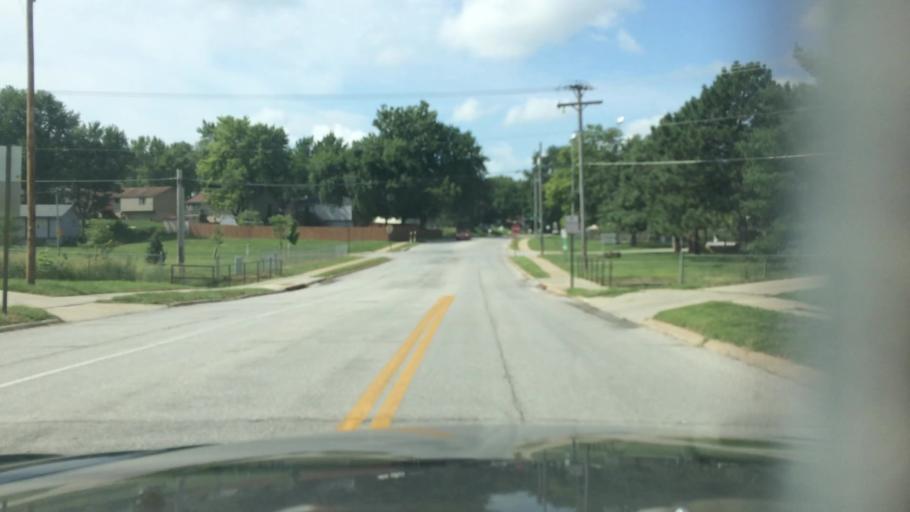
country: US
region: Nebraska
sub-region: Sarpy County
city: La Vista
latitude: 41.1815
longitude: -96.0334
